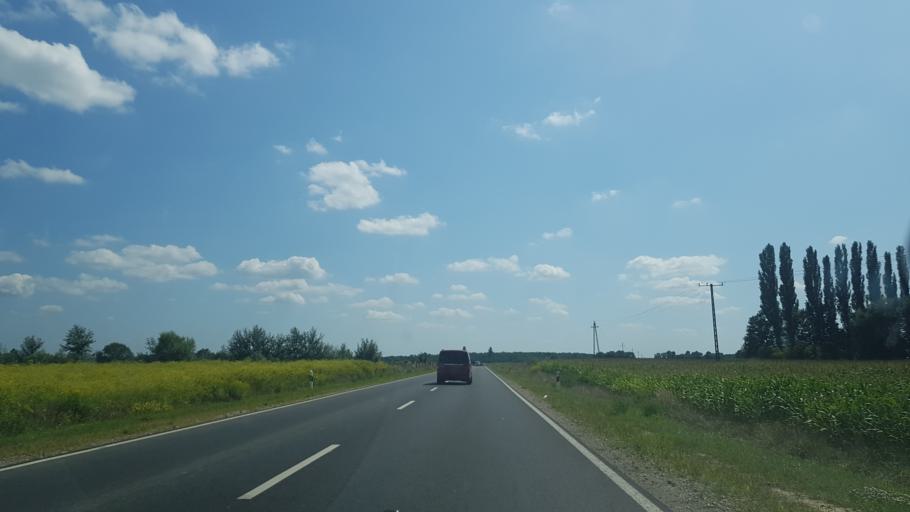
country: HU
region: Somogy
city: Marcali
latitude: 46.5799
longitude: 17.4312
